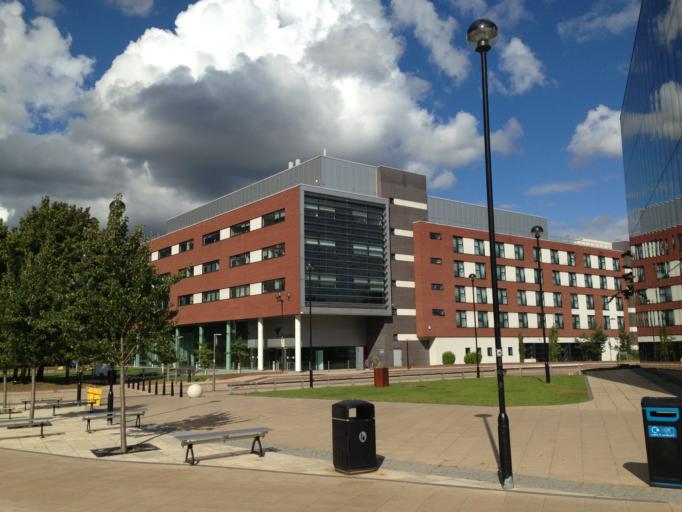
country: GB
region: England
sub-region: City and Borough of Birmingham
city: Birmingham
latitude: 52.4852
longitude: -1.8888
